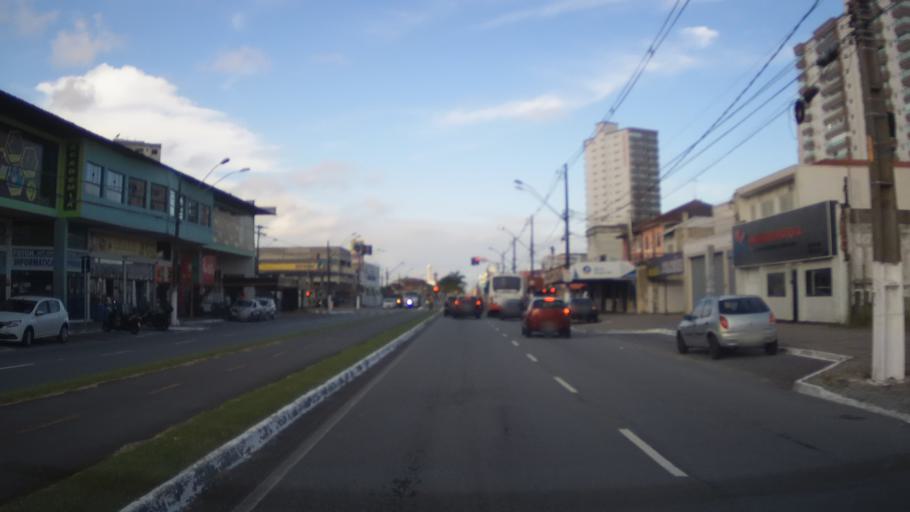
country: BR
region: Sao Paulo
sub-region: Mongagua
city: Mongagua
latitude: -24.0473
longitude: -46.5304
